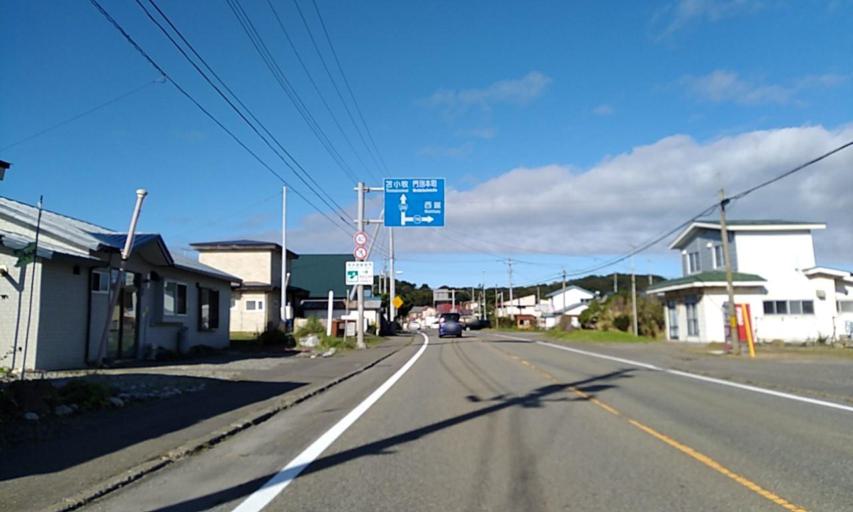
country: JP
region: Hokkaido
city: Shizunai-furukawacho
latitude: 42.2679
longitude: 142.5020
